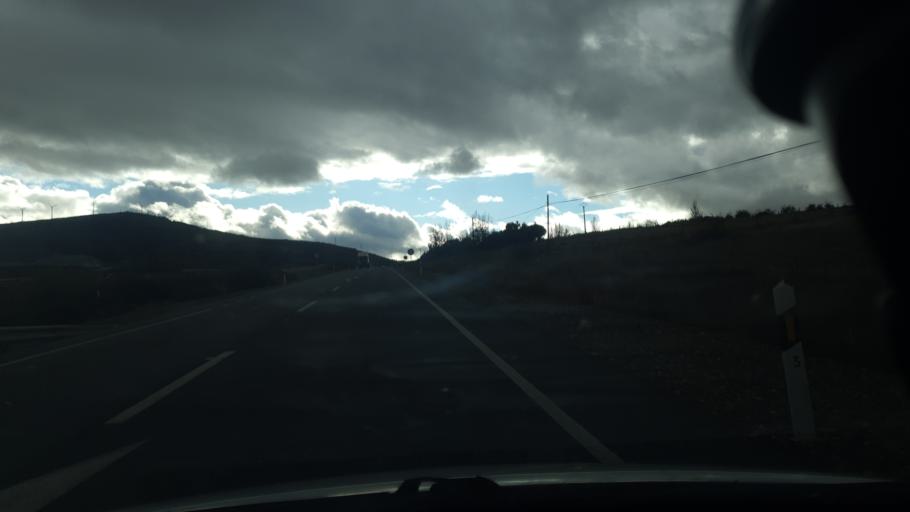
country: ES
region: Castille and Leon
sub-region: Provincia de Segovia
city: Villacastin
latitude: 40.7459
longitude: -4.4631
